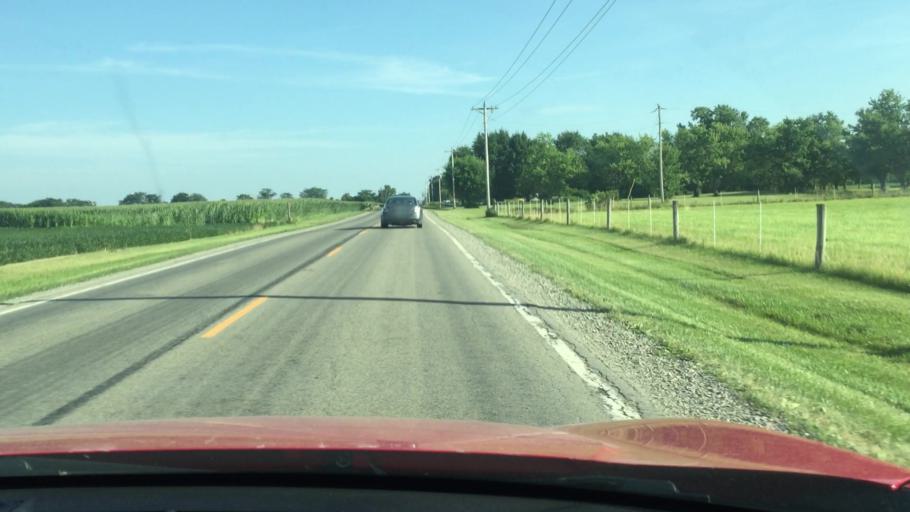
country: US
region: Ohio
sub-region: Hardin County
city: Ada
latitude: 40.6570
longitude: -83.8501
